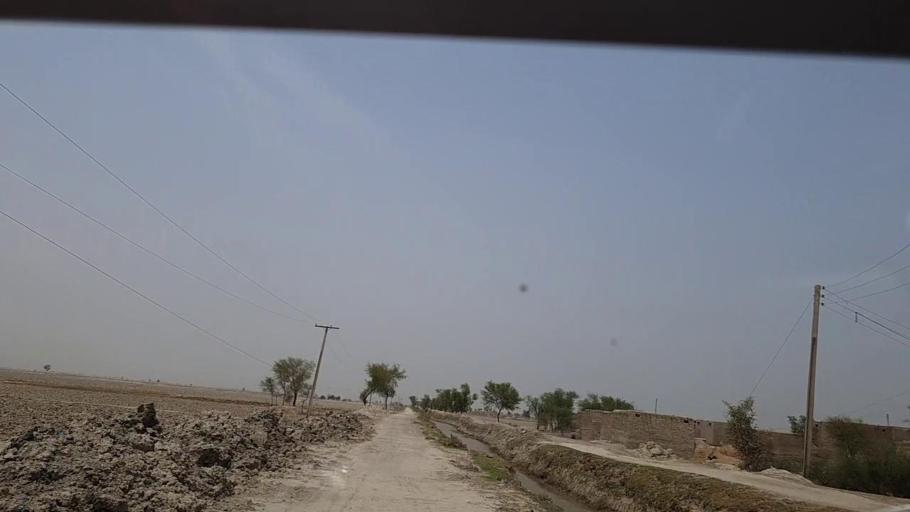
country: PK
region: Sindh
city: Khairpur Nathan Shah
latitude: 27.0470
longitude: 67.6190
